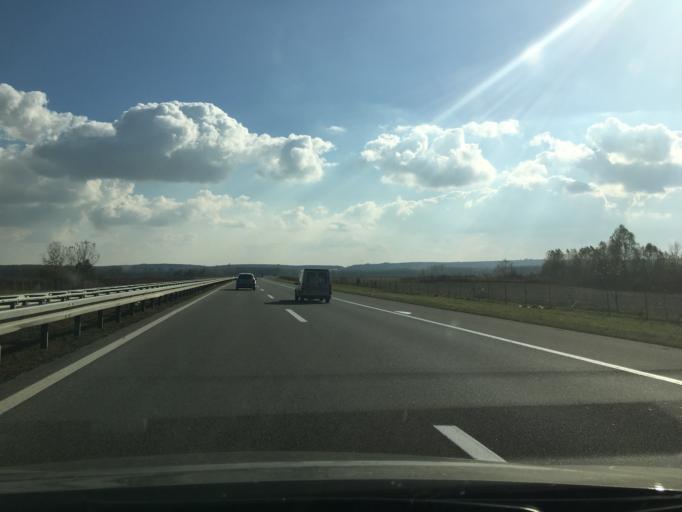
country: RS
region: Autonomna Pokrajina Vojvodina
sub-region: Juznobacki Okrug
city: Kovilj
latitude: 45.2052
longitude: 20.0706
